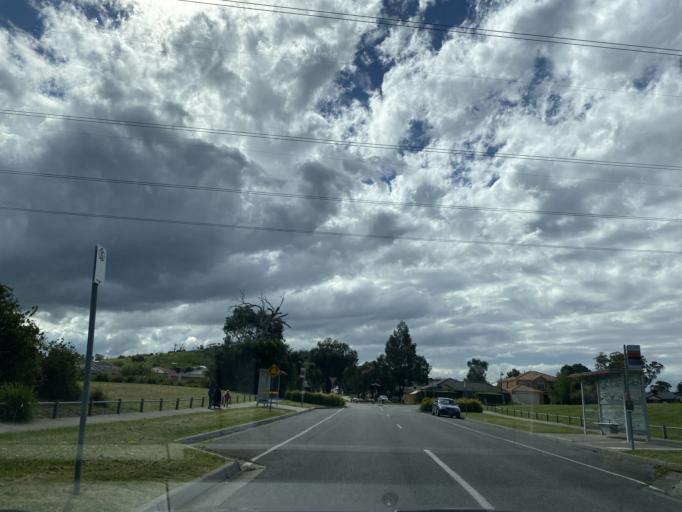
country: AU
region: Victoria
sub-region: Whittlesea
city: Mernda
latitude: -37.6303
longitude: 145.0935
